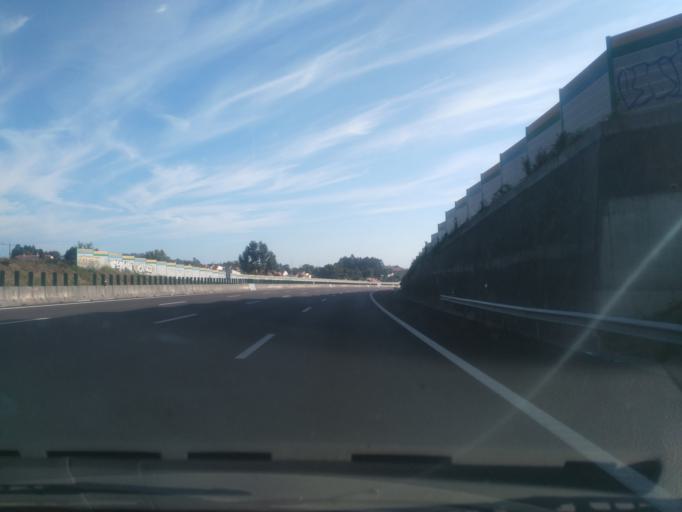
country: PT
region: Porto
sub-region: Vila Nova de Gaia
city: Grijo
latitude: 41.0282
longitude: -8.5727
